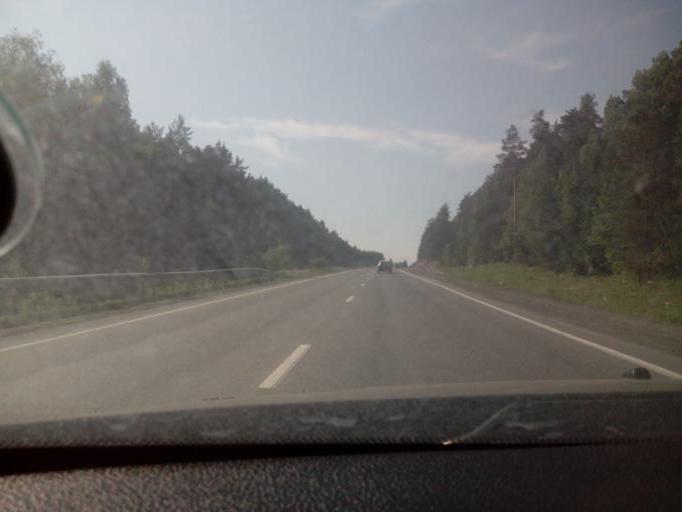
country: RU
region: Sverdlovsk
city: Iset'
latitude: 57.1023
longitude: 60.3572
